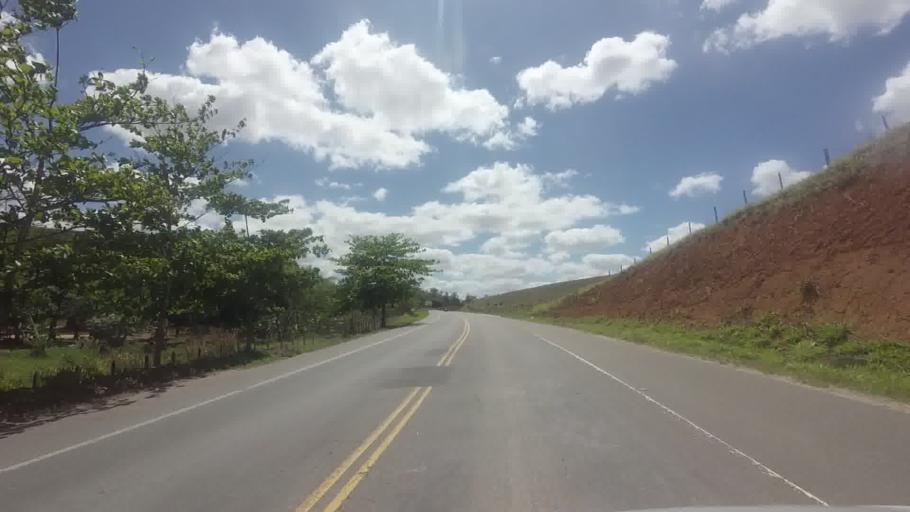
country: BR
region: Minas Gerais
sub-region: Recreio
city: Recreio
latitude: -21.6583
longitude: -42.3713
